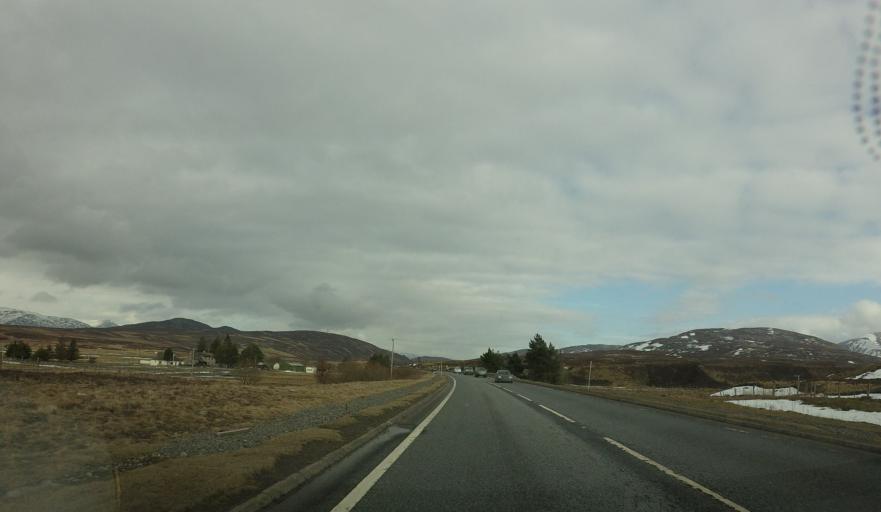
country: GB
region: Scotland
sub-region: Highland
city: Kingussie
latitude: 56.9529
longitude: -4.2125
